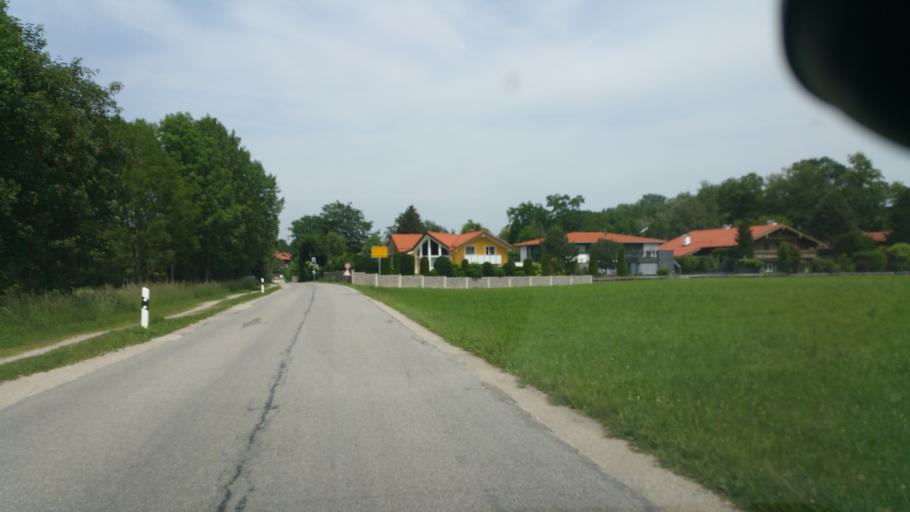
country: DE
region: Bavaria
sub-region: Upper Bavaria
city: Aschau im Chiemgau
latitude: 47.7895
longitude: 12.3259
